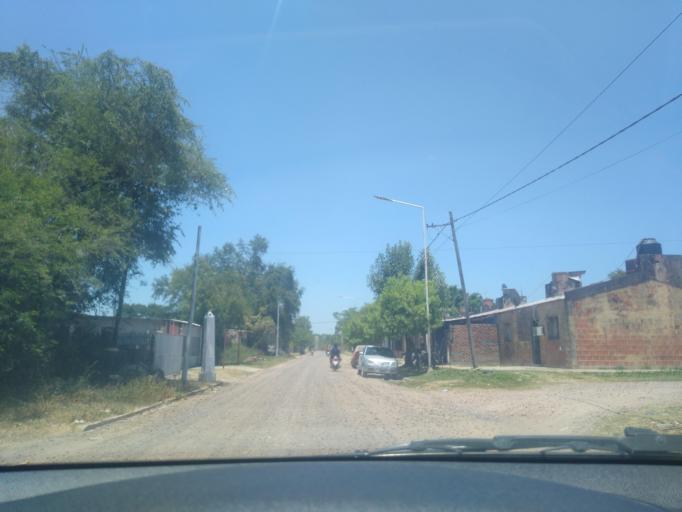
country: AR
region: Chaco
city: Puerto Tirol
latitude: -27.3835
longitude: -59.0877
